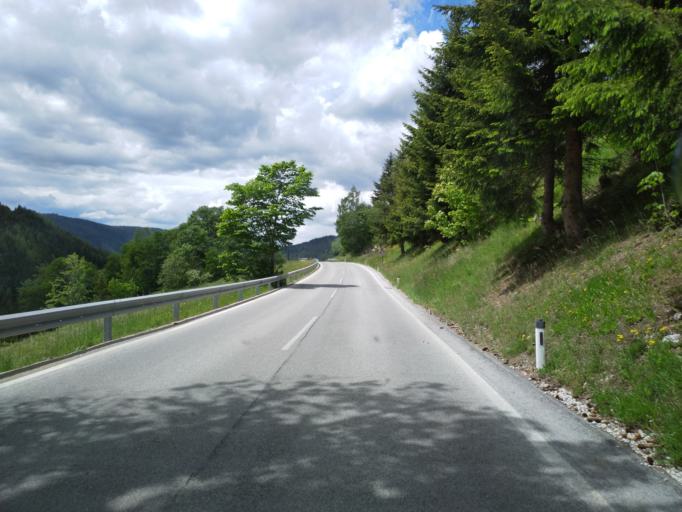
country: AT
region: Salzburg
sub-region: Politischer Bezirk Sankt Johann im Pongau
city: Filzmoos
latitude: 47.4270
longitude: 13.5924
